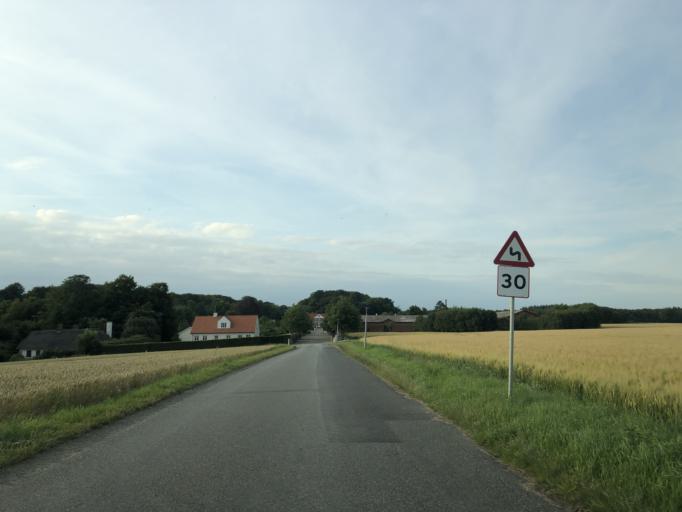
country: DK
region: South Denmark
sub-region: Fredericia Kommune
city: Taulov
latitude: 55.5966
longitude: 9.6048
